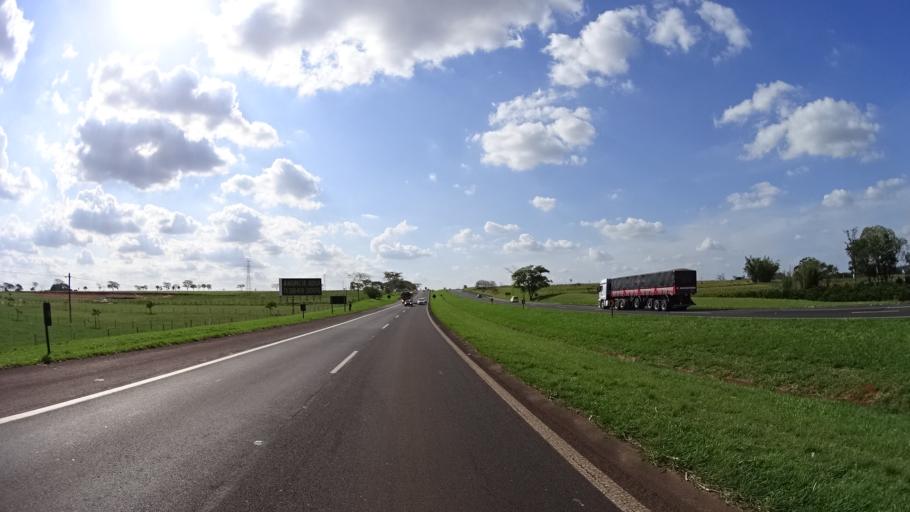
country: BR
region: Sao Paulo
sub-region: Guapiacu
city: Guapiacu
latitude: -20.9566
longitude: -49.2495
